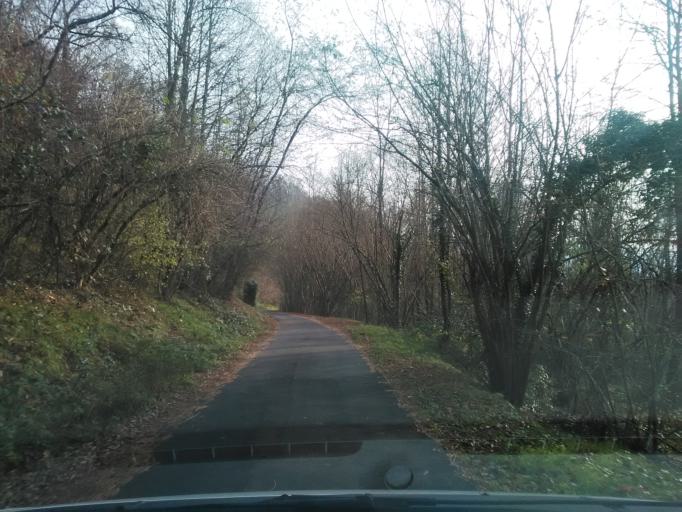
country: IT
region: Piedmont
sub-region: Provincia di Vercelli
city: Guardabosone
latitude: 45.7027
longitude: 8.2404
